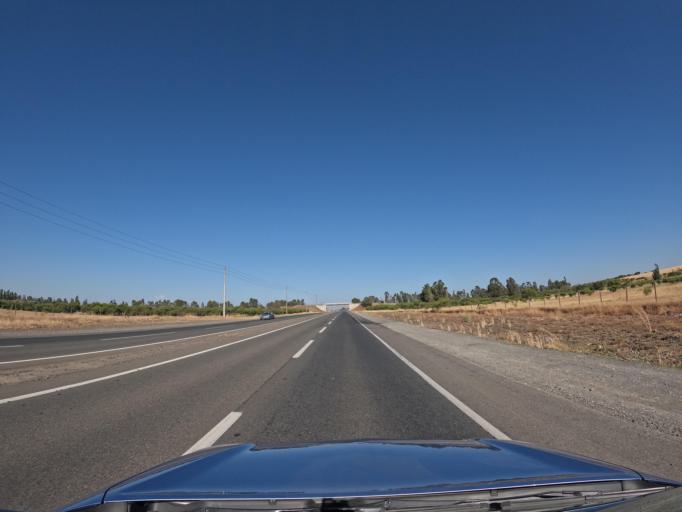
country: CL
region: Biobio
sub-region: Provincia de Nuble
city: Bulnes
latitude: -36.6589
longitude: -72.2809
